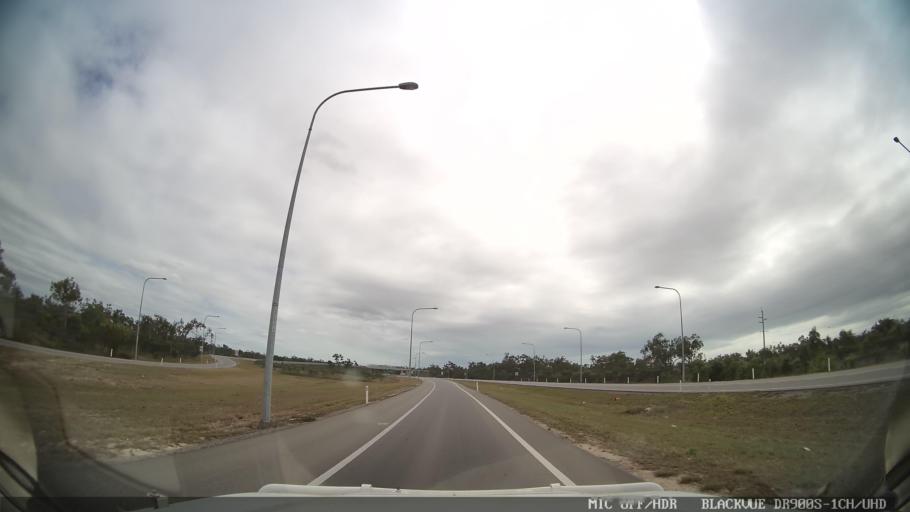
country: AU
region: Queensland
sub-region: Townsville
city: Bohle Plains
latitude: -19.2996
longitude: 146.6952
